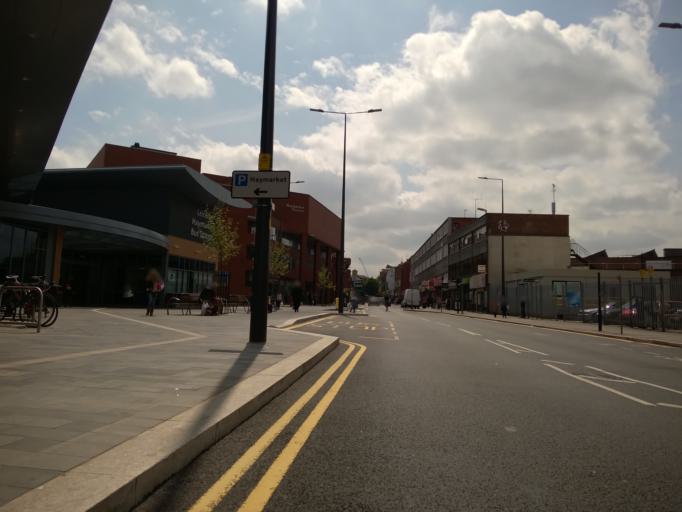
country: GB
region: England
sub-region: City of Leicester
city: Leicester
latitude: 52.6384
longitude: -1.1318
